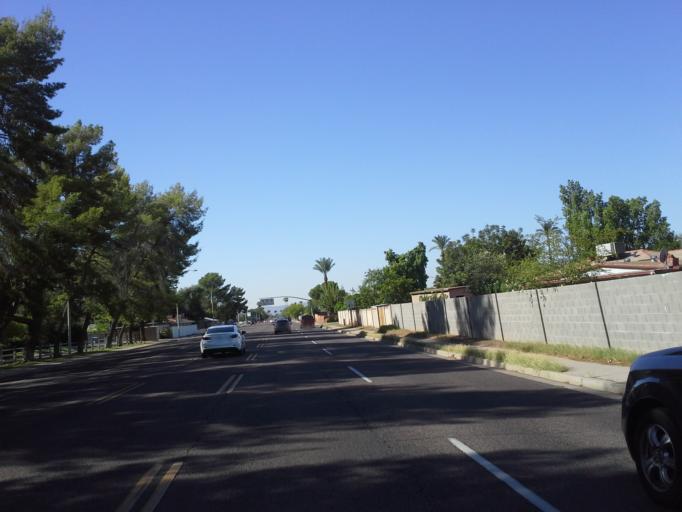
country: US
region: Arizona
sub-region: Maricopa County
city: Phoenix
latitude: 33.5204
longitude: -112.0825
